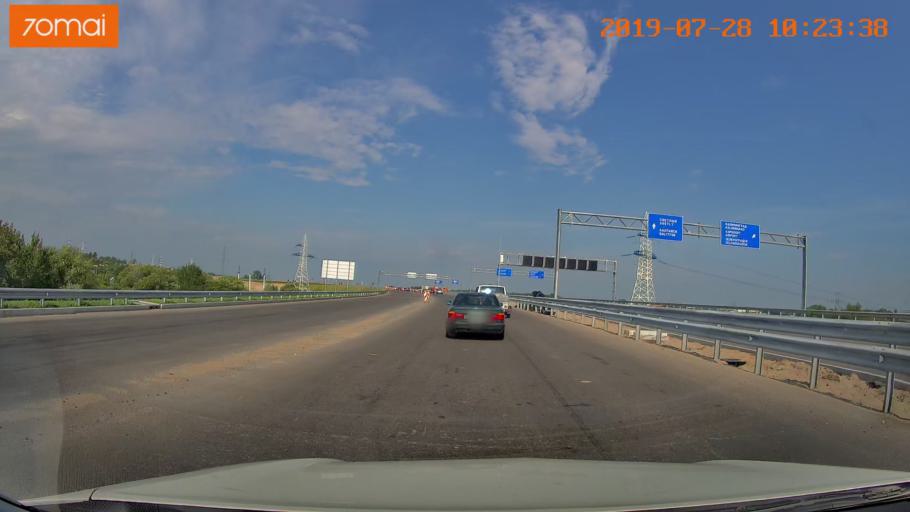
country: RU
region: Kaliningrad
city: Maloye Isakovo
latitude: 54.7672
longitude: 20.5575
